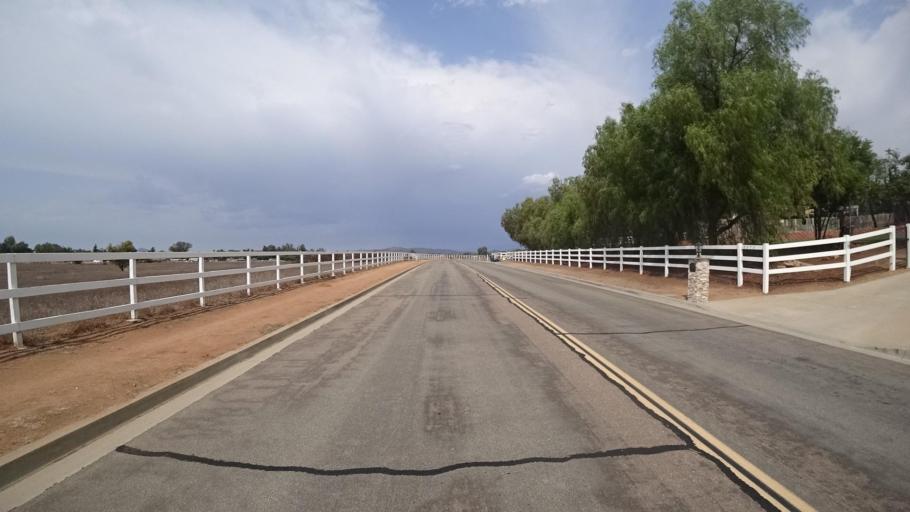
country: US
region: California
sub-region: San Diego County
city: Ramona
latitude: 33.0048
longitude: -116.8949
